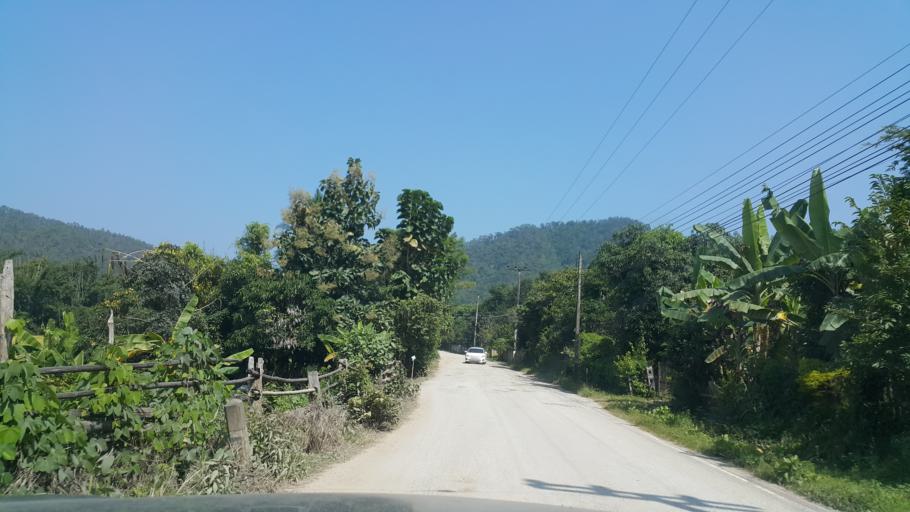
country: TH
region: Chiang Mai
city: Samoeng
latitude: 18.9078
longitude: 98.6004
